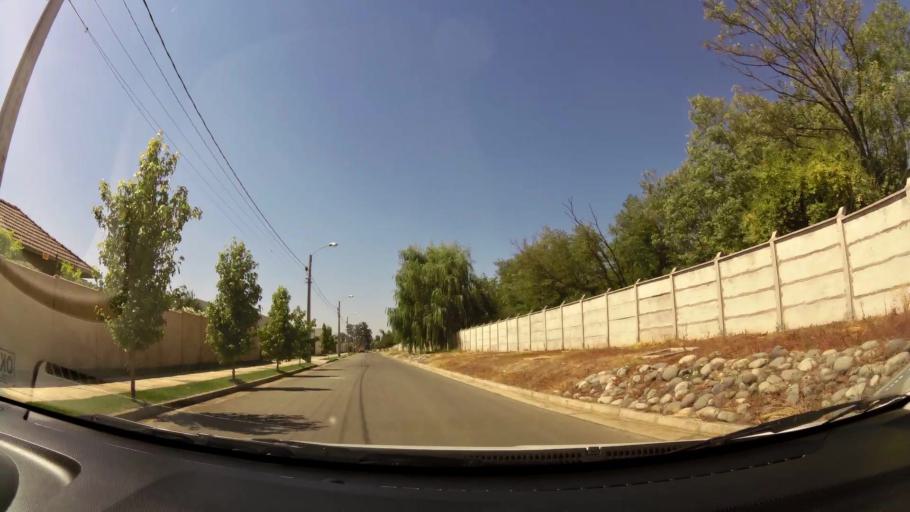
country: CL
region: Maule
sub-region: Provincia de Talca
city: Talca
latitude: -35.4407
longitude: -71.5955
